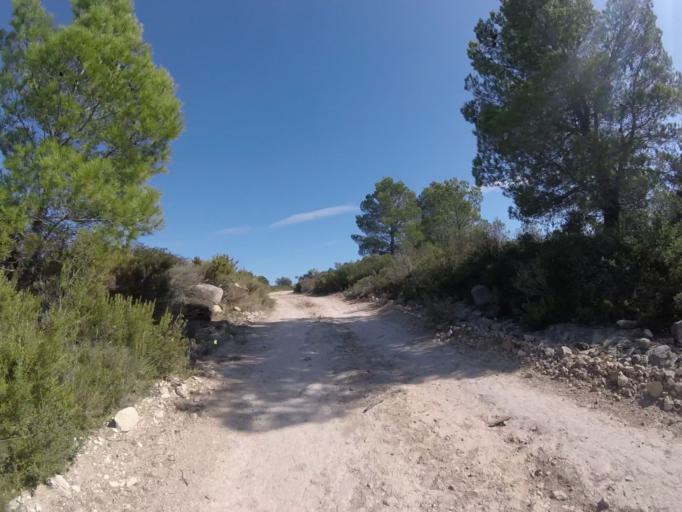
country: ES
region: Valencia
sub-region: Provincia de Castello
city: Sarratella
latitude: 40.2715
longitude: 0.0274
